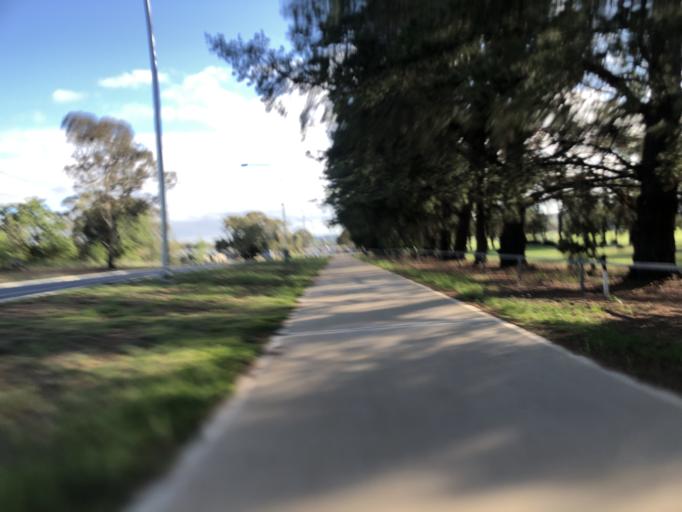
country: AU
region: New South Wales
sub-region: Orange Municipality
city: Orange
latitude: -33.3106
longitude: 149.0958
